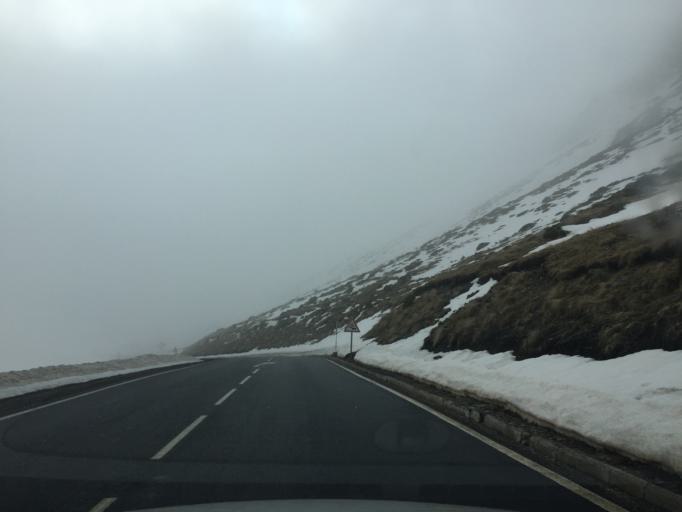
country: ES
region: Aragon
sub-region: Provincia de Huesca
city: Bielsa
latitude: 42.7521
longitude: 0.1909
